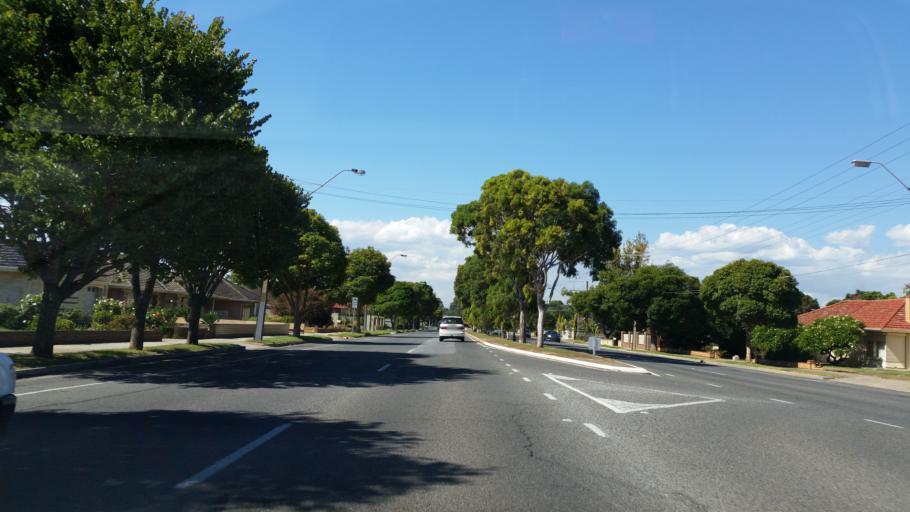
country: AU
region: South Australia
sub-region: Charles Sturt
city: Henley Beach
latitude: -34.9266
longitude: 138.5118
